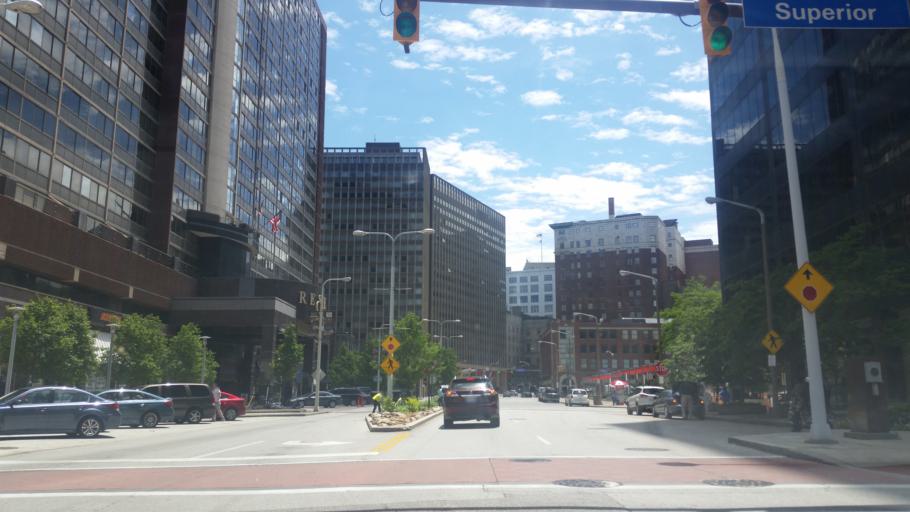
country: US
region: Ohio
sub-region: Cuyahoga County
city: Cleveland
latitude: 41.5034
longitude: -81.6863
